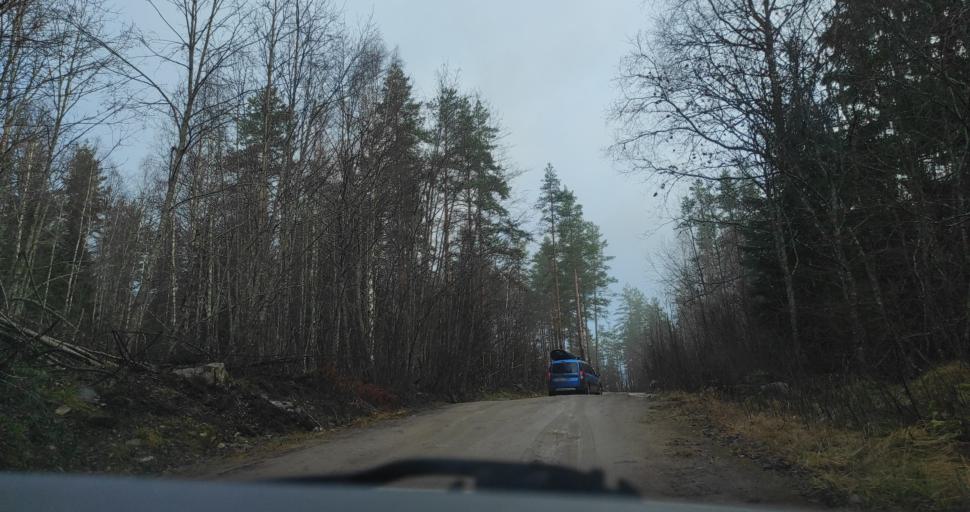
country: RU
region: Republic of Karelia
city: Pitkyaranta
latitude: 61.7388
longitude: 31.3898
